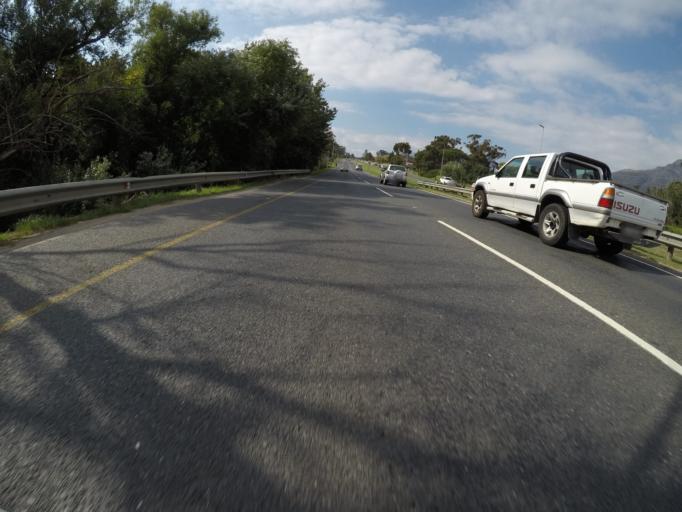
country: ZA
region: Western Cape
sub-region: Cape Winelands District Municipality
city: Stellenbosch
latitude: -33.9724
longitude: 18.8426
